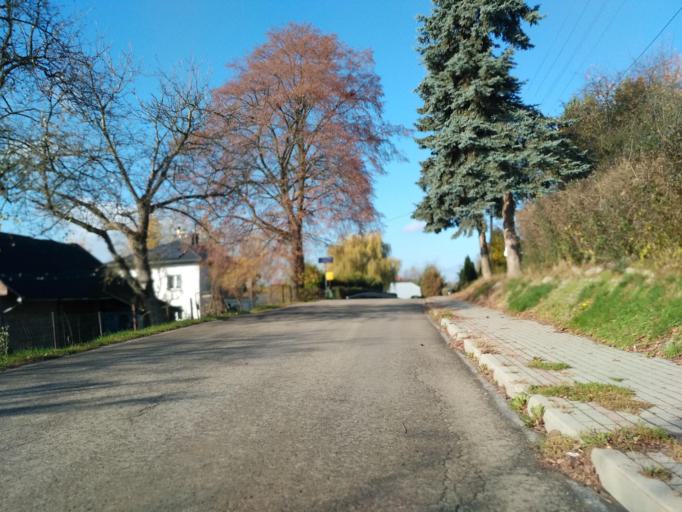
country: PL
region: Subcarpathian Voivodeship
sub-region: Powiat rzeszowski
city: Zglobien
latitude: 50.0246
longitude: 21.8723
